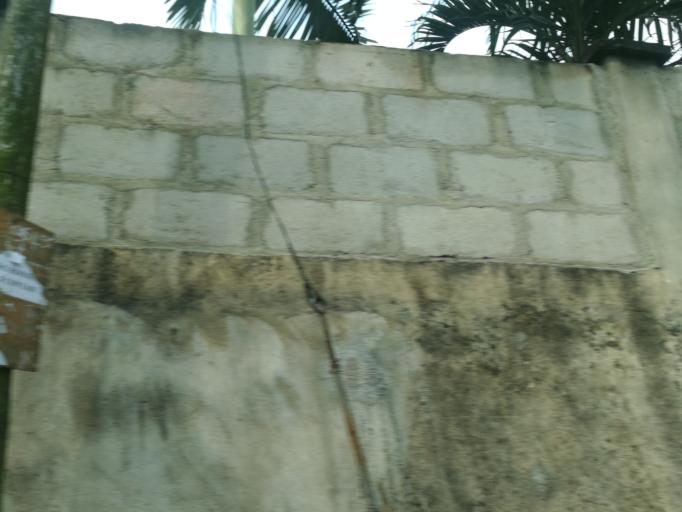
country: NG
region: Rivers
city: Port Harcourt
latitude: 4.8716
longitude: 6.9834
